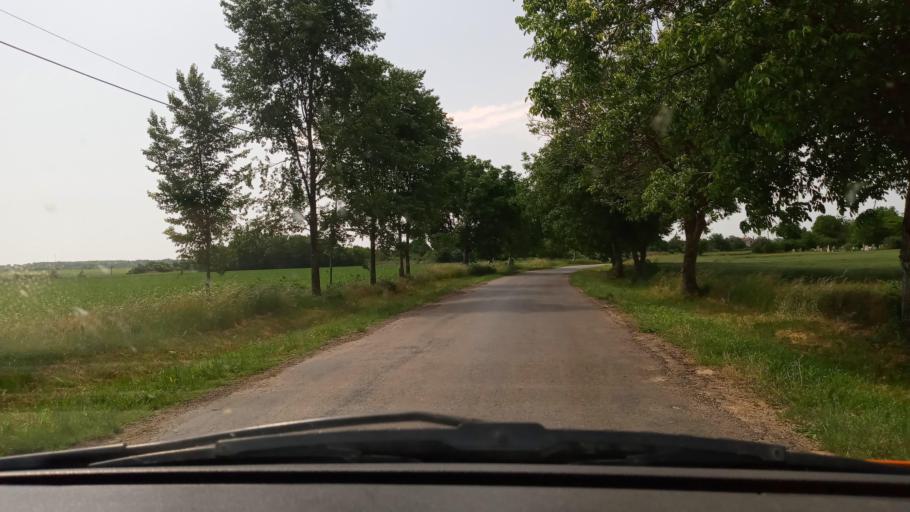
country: HU
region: Baranya
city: Szentlorinc
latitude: 45.9960
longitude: 18.0366
